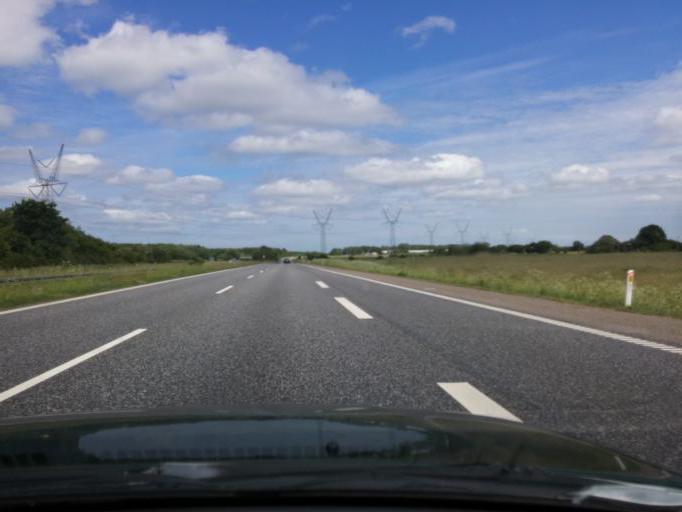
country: DK
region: South Denmark
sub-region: Fredericia Kommune
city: Taulov
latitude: 55.5388
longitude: 9.6464
